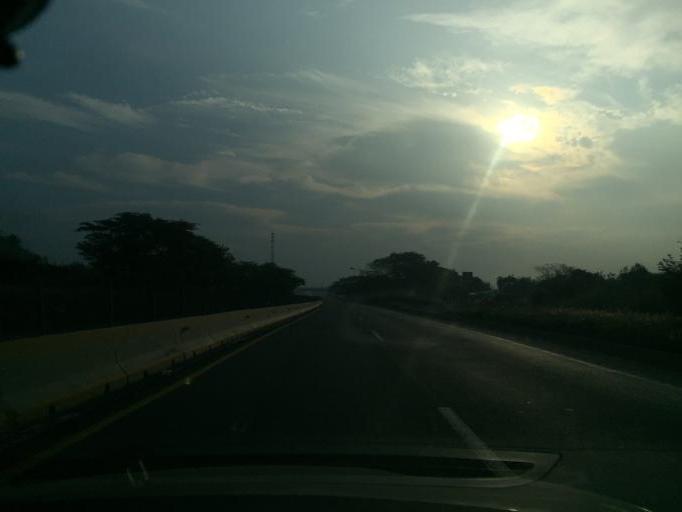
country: MX
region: Veracruz
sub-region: Omealca
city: Mata Tenatito (Casco Hacienda)
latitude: 18.7895
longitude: -96.5626
